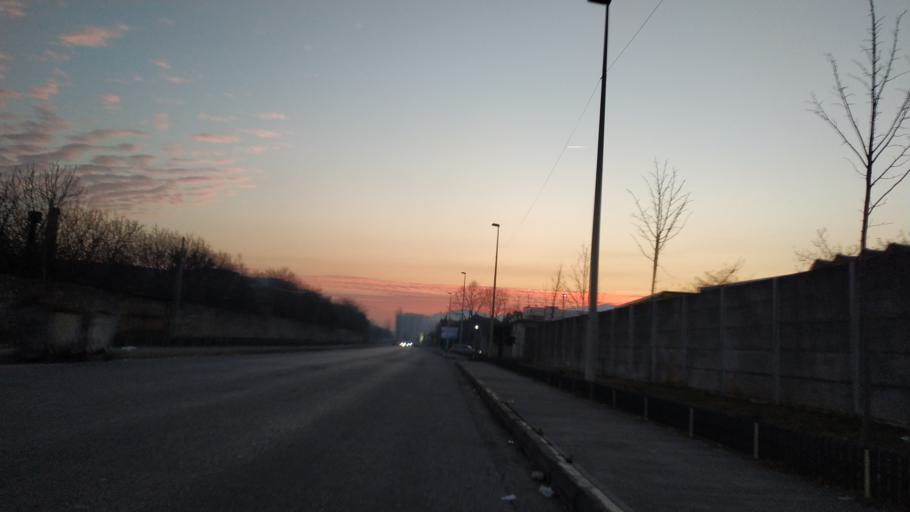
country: AL
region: Shkoder
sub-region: Rrethi i Shkodres
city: Shkoder
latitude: 42.0824
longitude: 19.5268
